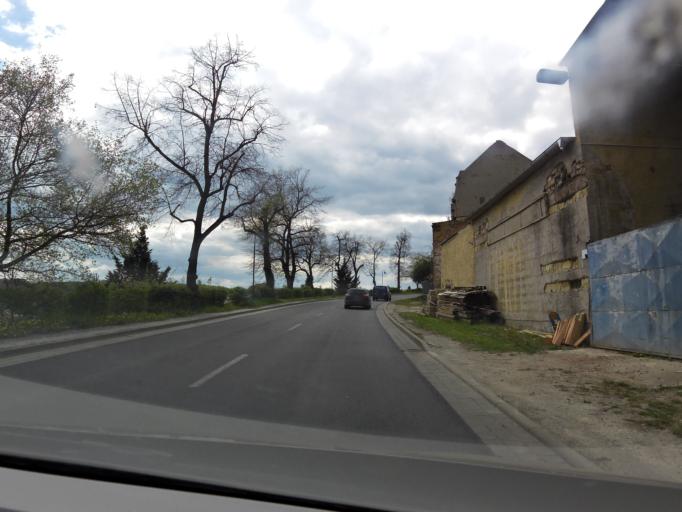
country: DE
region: Saxony-Anhalt
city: Bad Kosen
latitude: 51.1325
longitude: 11.7147
